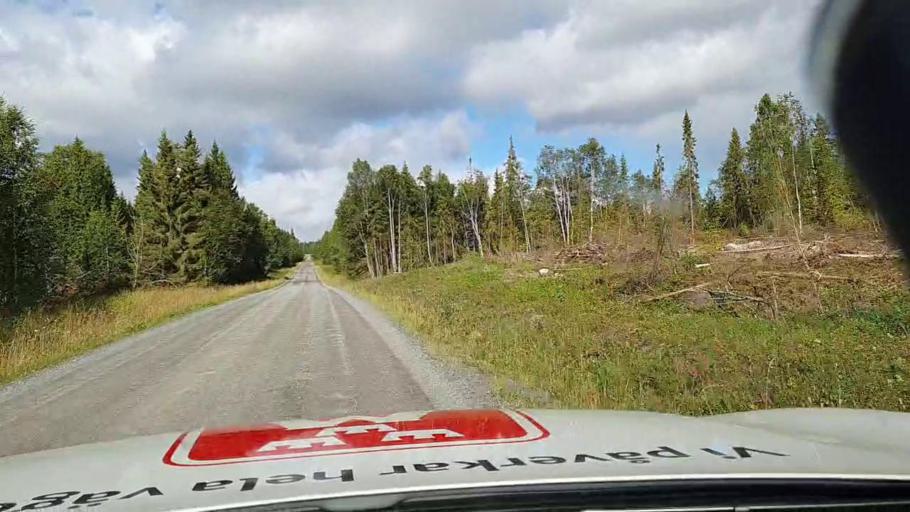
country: SE
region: Jaemtland
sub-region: Stroemsunds Kommun
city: Stroemsund
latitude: 63.7624
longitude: 15.2345
